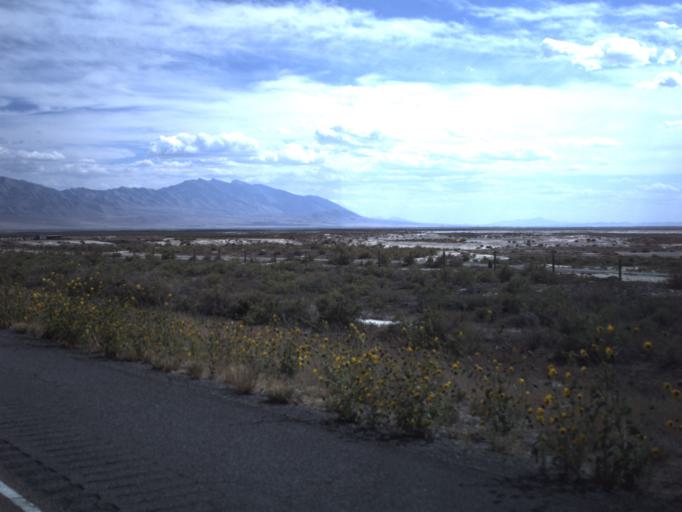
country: US
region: Utah
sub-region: Tooele County
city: Grantsville
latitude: 40.7760
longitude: -112.8058
